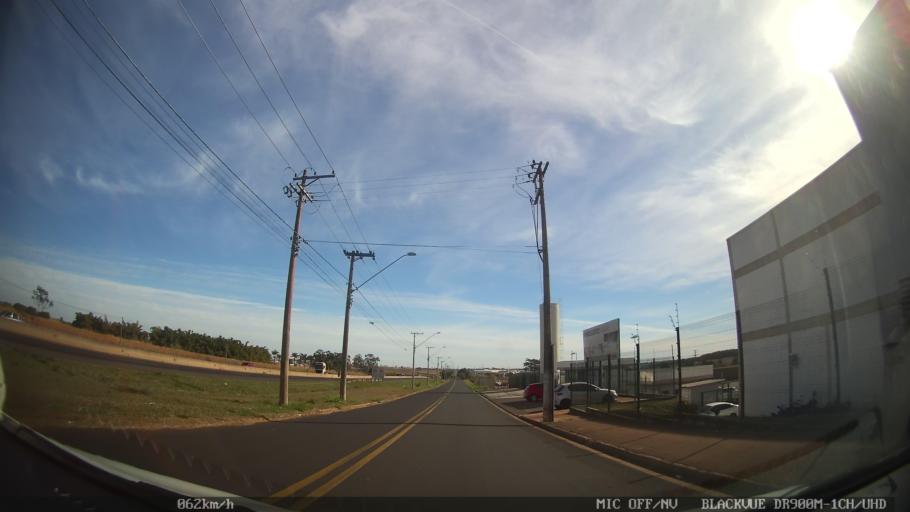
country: BR
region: Sao Paulo
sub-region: Sao Jose Do Rio Preto
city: Sao Jose do Rio Preto
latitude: -20.7934
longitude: -49.3088
